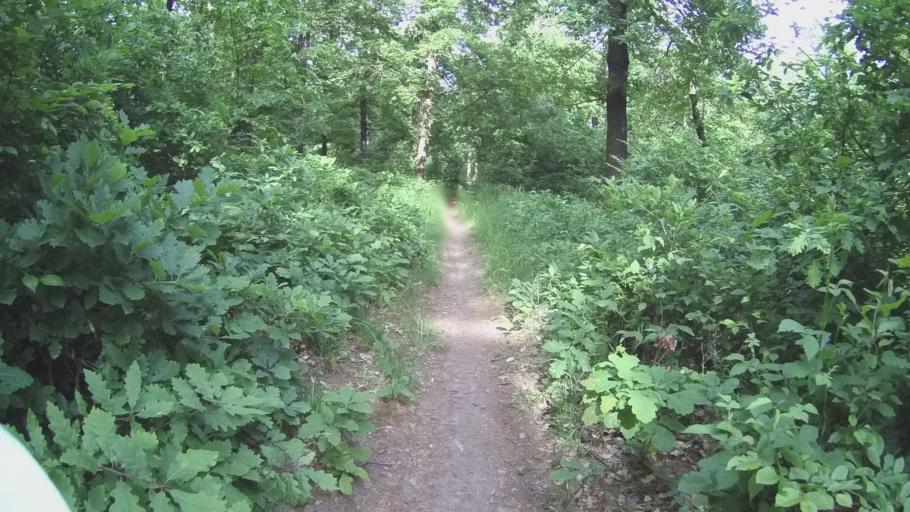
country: CZ
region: Central Bohemia
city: Zdiby
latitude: 50.2041
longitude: 14.4494
